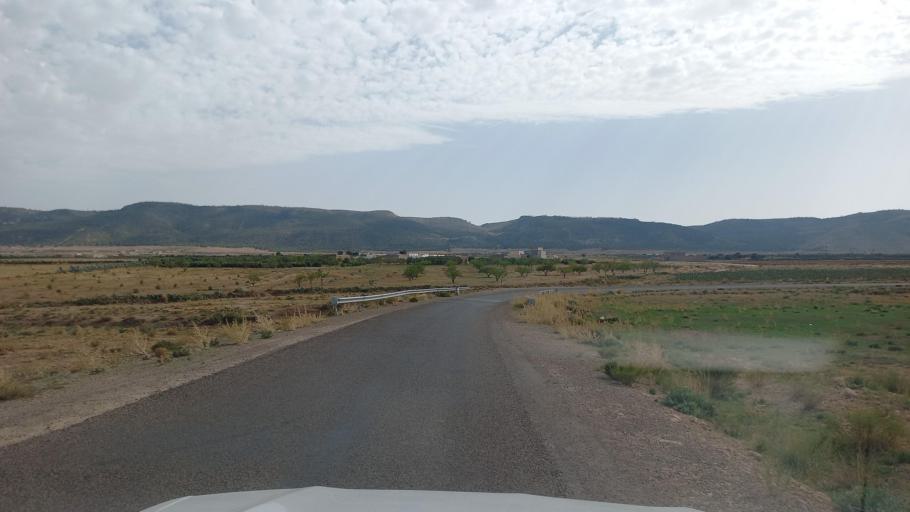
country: TN
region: Al Qasrayn
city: Kasserine
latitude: 35.3588
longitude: 8.8297
